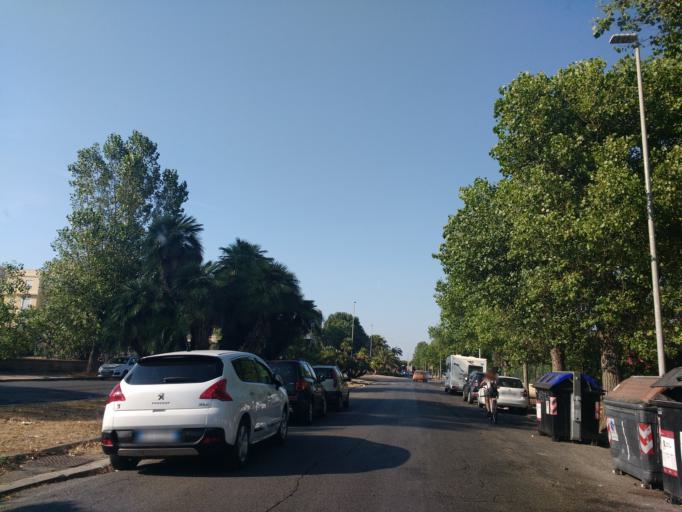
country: IT
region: Latium
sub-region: Citta metropolitana di Roma Capitale
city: Lido di Ostia
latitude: 41.7277
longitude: 12.2873
